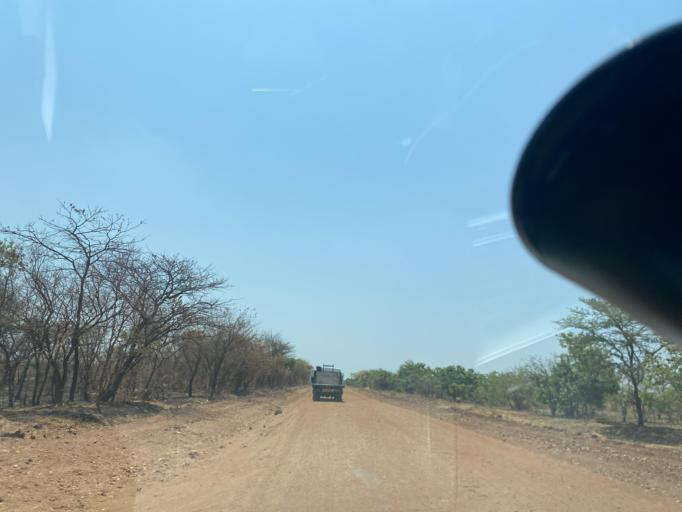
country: ZM
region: Lusaka
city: Lusaka
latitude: -15.4578
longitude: 27.9345
